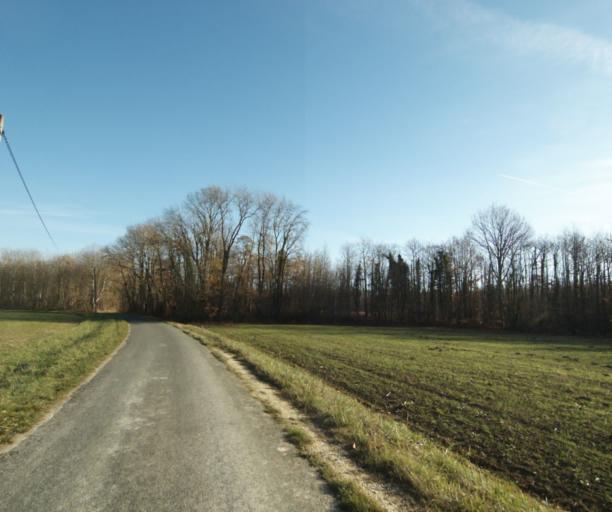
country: FR
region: Poitou-Charentes
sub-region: Departement de la Charente-Maritime
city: Burie
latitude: 45.7764
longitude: -0.4407
